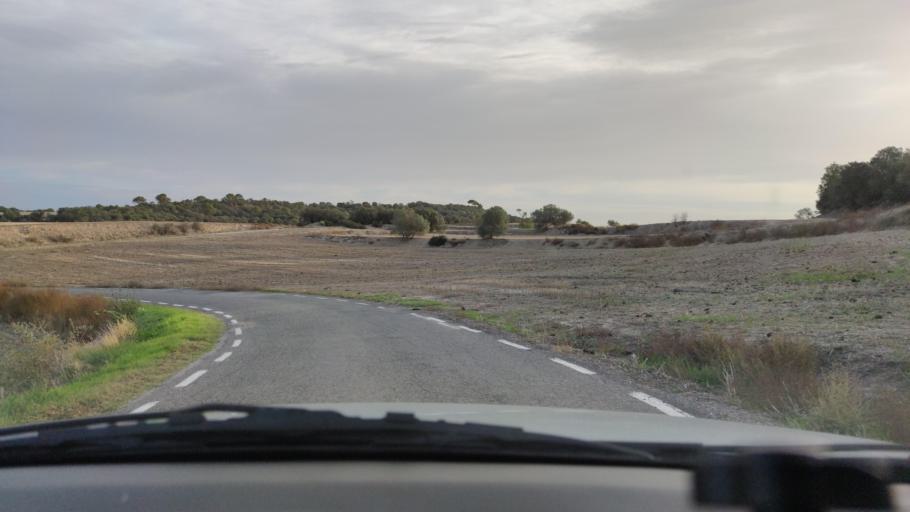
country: ES
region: Catalonia
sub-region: Provincia de Lleida
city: Agramunt
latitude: 41.8382
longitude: 1.0918
